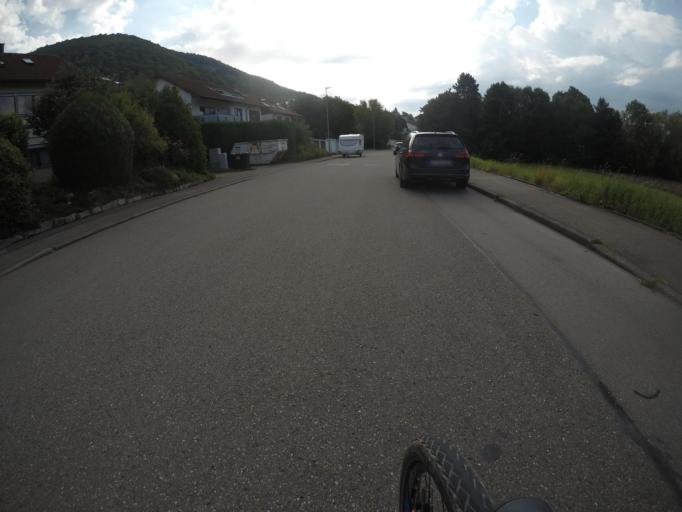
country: DE
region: Baden-Wuerttemberg
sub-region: Tuebingen Region
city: Bad Urach
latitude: 48.5087
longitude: 9.3757
